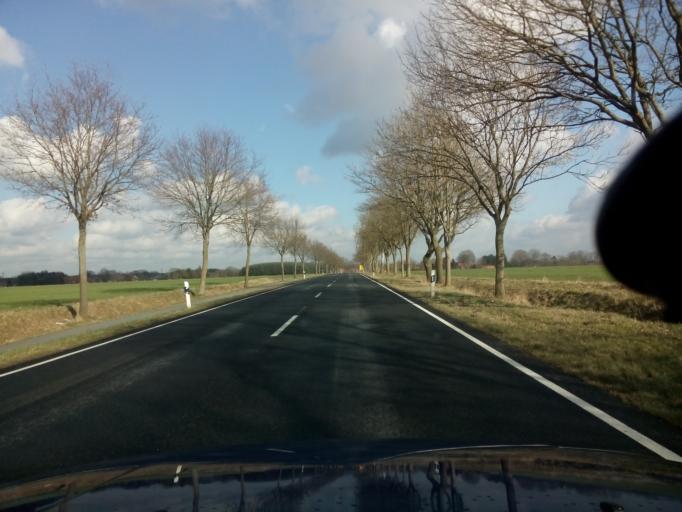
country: DE
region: Lower Saxony
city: Gnarrenburg
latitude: 53.3767
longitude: 8.9541
